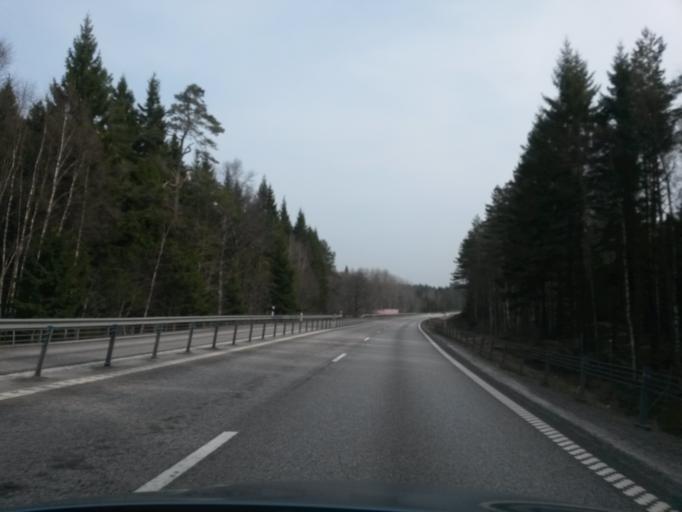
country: SE
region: Vaestra Goetaland
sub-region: Gullspangs Kommun
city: Anderstorp
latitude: 58.8916
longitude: 14.3147
